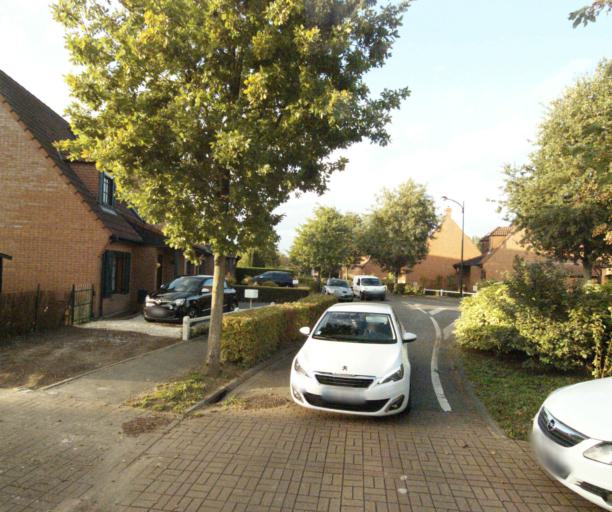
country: FR
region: Nord-Pas-de-Calais
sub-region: Departement du Nord
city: Sequedin
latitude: 50.6255
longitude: 2.9787
